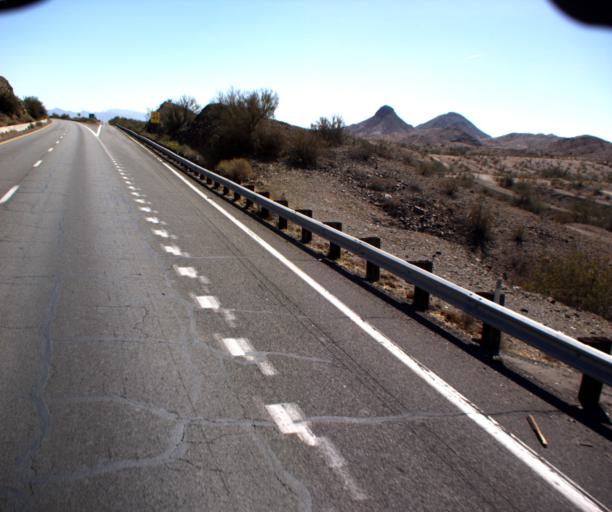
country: US
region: Arizona
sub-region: La Paz County
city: Quartzsite
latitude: 33.6468
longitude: -114.3397
